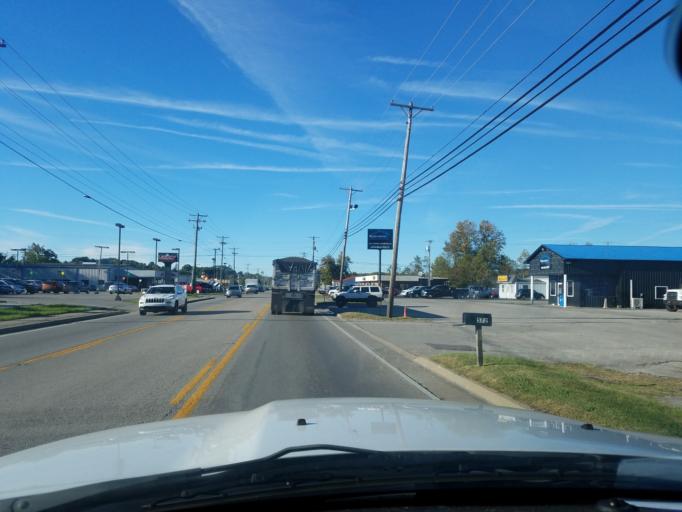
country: US
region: Kentucky
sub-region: Laurel County
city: London
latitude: 37.0992
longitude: -84.0682
